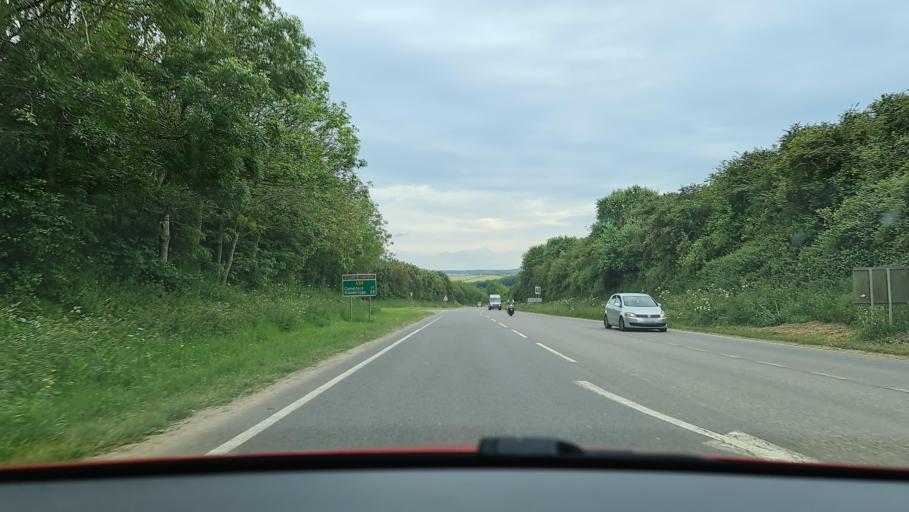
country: GB
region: England
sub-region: Cornwall
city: Bude
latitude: 50.8154
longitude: -4.5287
